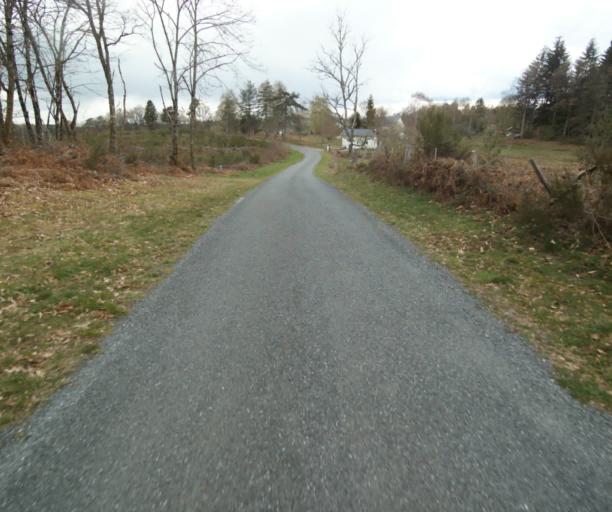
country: FR
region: Limousin
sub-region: Departement de la Correze
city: Correze
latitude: 45.2936
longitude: 1.9238
